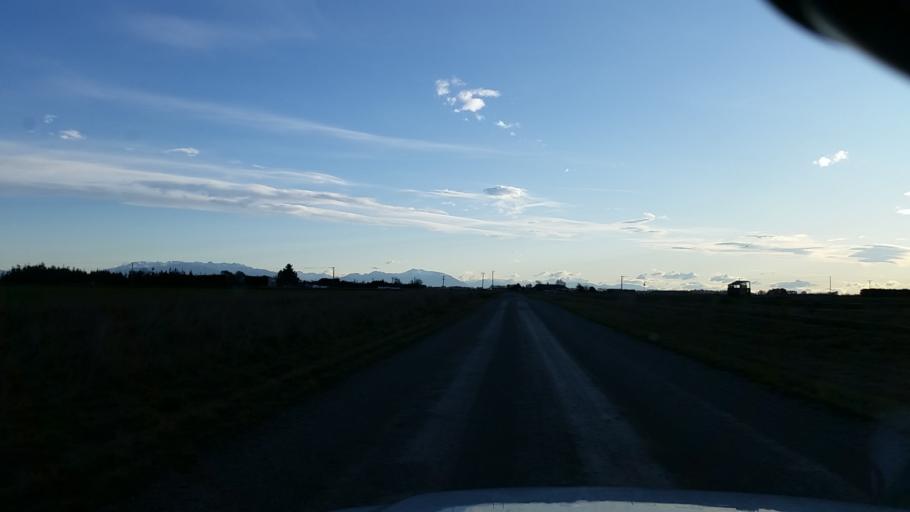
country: NZ
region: Canterbury
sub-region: Ashburton District
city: Tinwald
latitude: -43.9787
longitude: 171.5077
